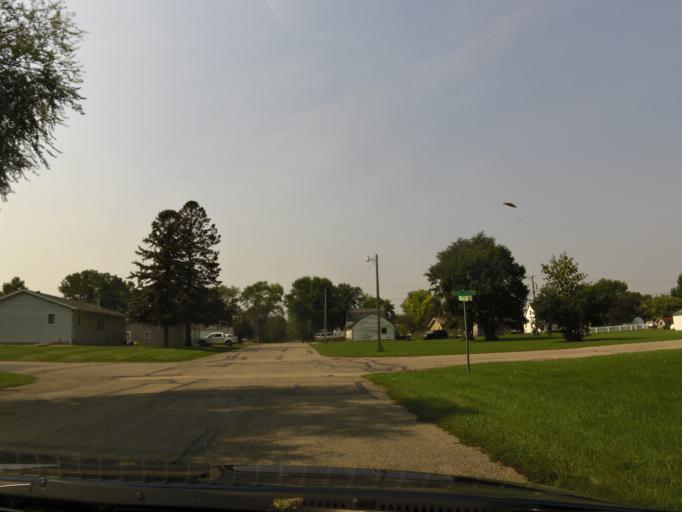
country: US
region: South Dakota
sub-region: Roberts County
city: Sisseton
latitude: 46.0733
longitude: -97.1442
